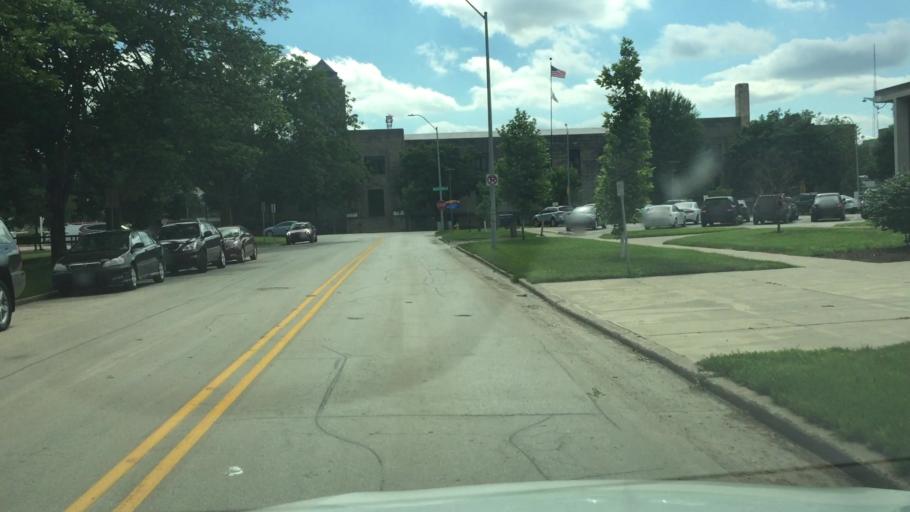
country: US
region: Iowa
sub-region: Polk County
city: Des Moines
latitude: 41.5909
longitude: -93.6159
